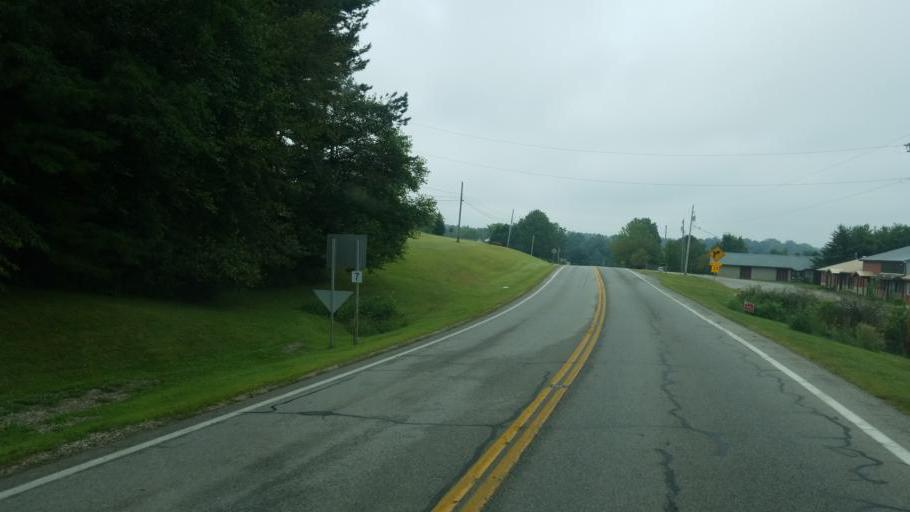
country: US
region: Ohio
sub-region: Knox County
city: Mount Vernon
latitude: 40.3433
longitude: -82.4685
